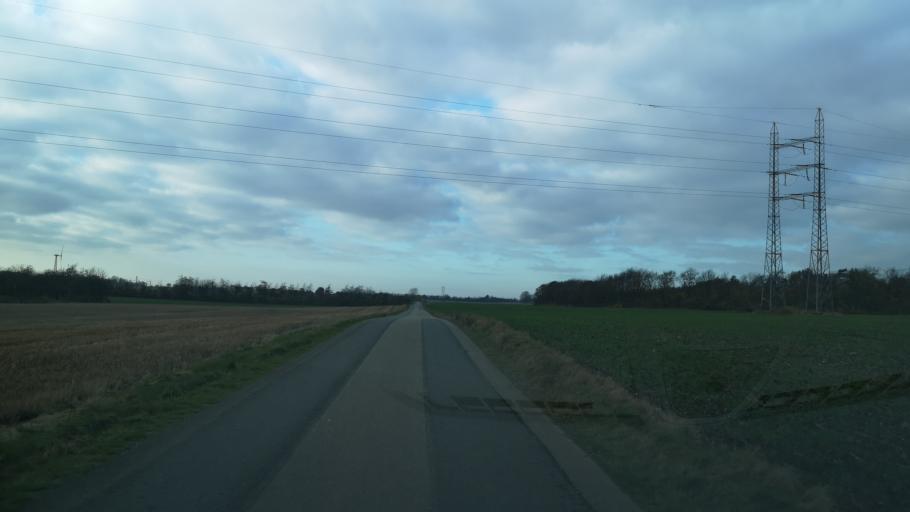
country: DK
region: Central Jutland
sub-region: Ringkobing-Skjern Kommune
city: Videbaek
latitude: 56.0413
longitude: 8.5938
